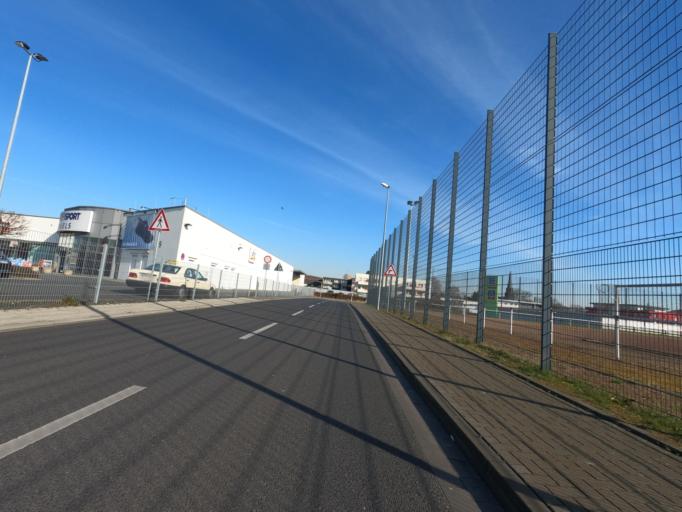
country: DE
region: North Rhine-Westphalia
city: Huckelhoven
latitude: 51.0540
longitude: 6.2208
